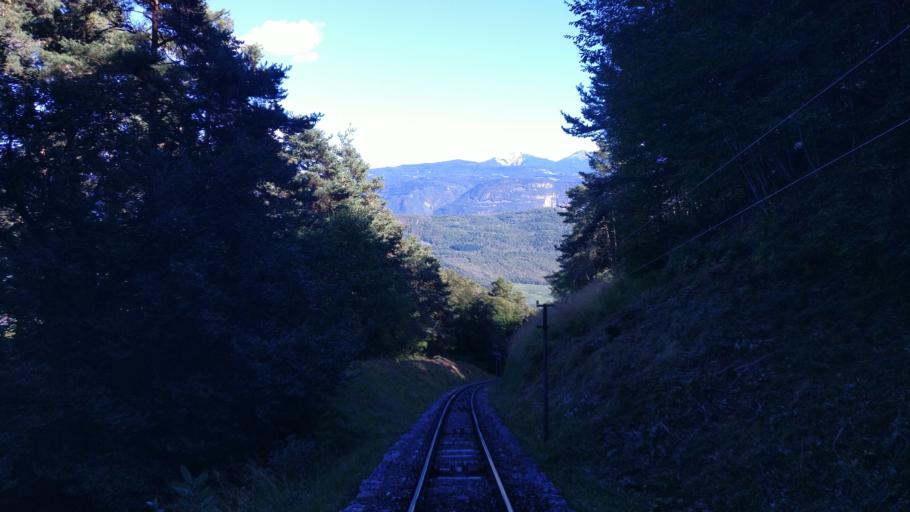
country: IT
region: Trentino-Alto Adige
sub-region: Bolzano
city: Caldaro sulla Strada del Vino
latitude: 46.4106
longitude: 11.2275
